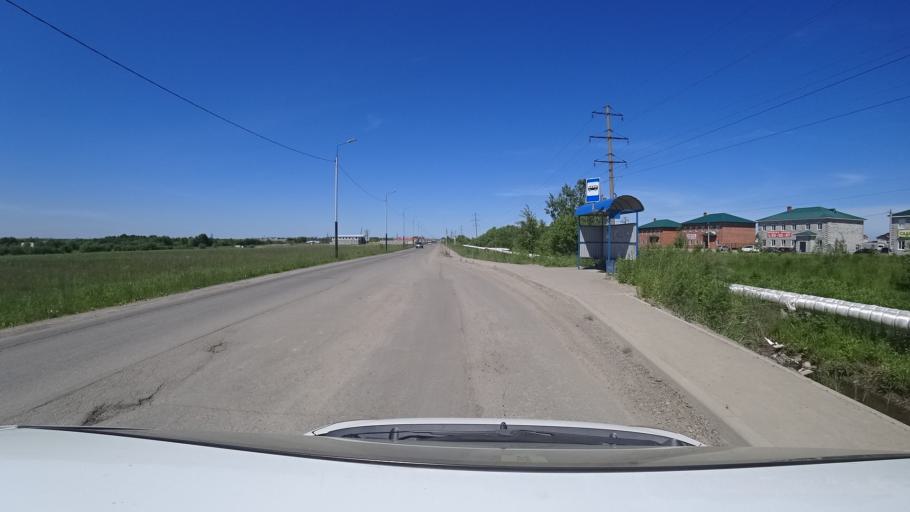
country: RU
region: Khabarovsk Krai
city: Topolevo
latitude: 48.4814
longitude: 135.1816
